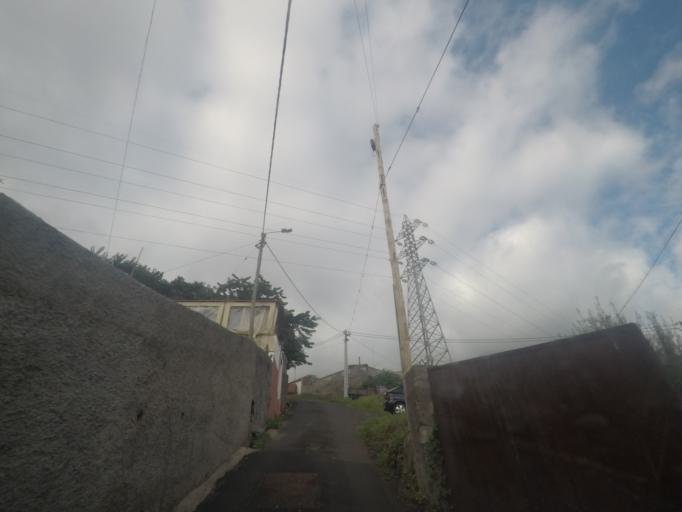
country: PT
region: Madeira
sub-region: Funchal
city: Nossa Senhora do Monte
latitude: 32.6695
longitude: -16.9418
